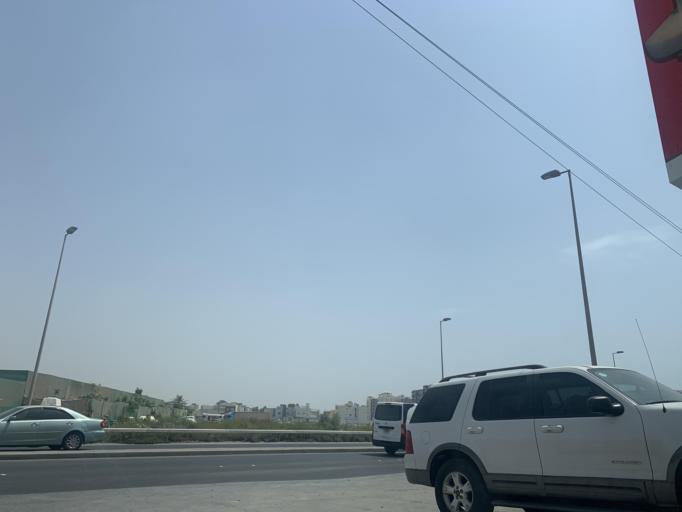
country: BH
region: Central Governorate
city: Madinat Hamad
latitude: 26.1406
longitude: 50.4894
